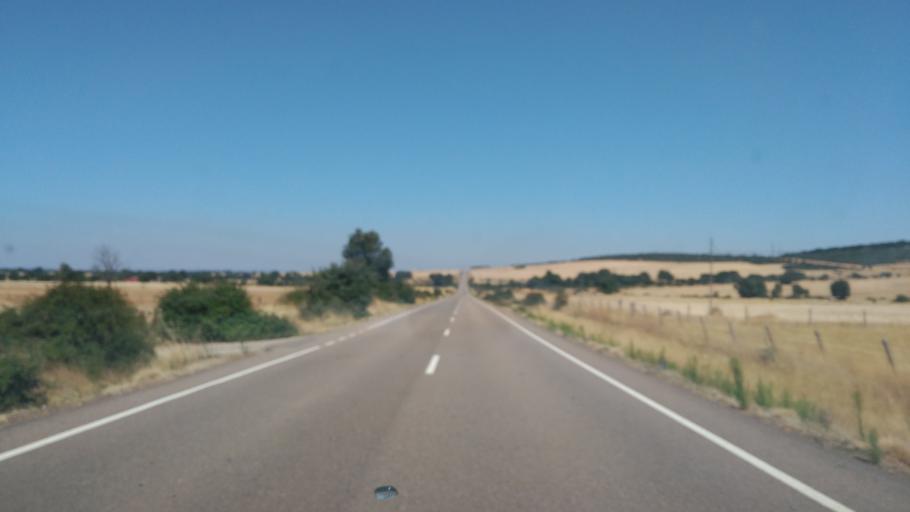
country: ES
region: Castille and Leon
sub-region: Provincia de Salamanca
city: Tamames
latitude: 40.6382
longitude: -6.1113
